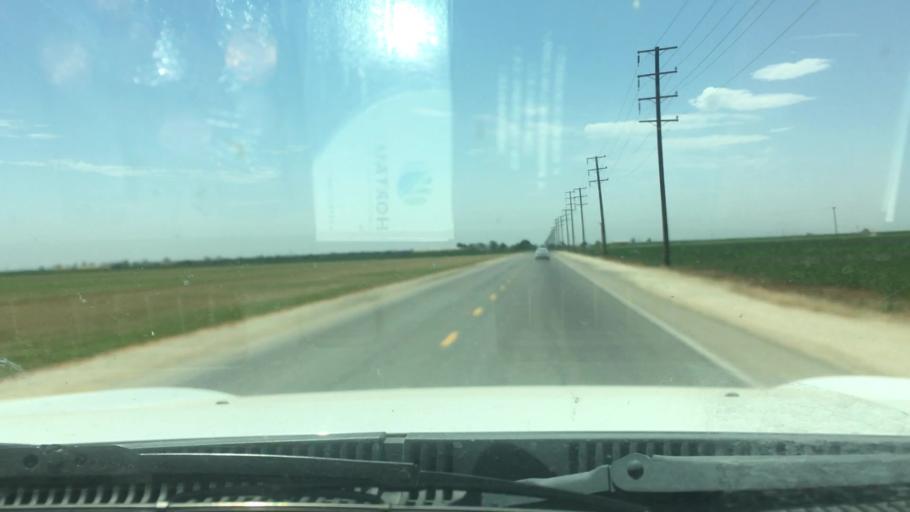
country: US
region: California
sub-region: Tulare County
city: Tipton
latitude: 36.0657
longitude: -119.2733
